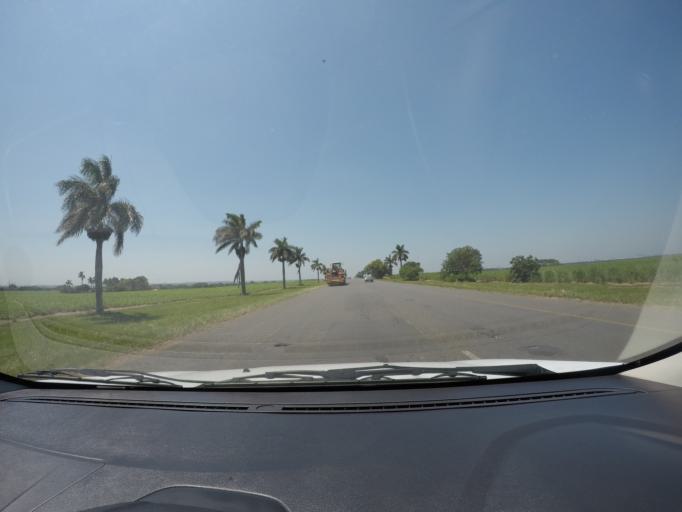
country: ZA
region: KwaZulu-Natal
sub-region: uThungulu District Municipality
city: Empangeni
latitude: -28.8129
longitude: 31.9552
